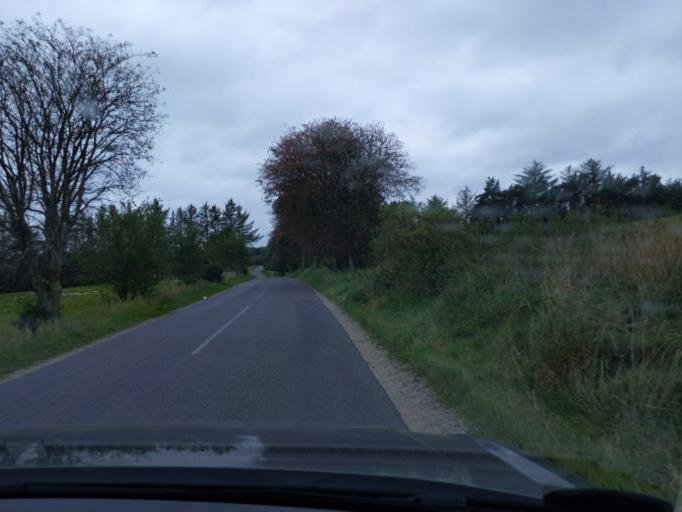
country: DK
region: North Denmark
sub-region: Mariagerfjord Kommune
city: Hobro
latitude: 56.5599
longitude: 9.7010
